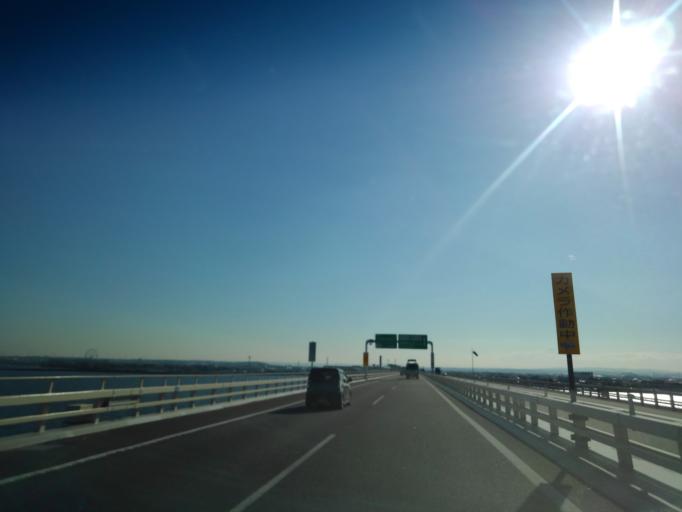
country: JP
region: Chiba
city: Kisarazu
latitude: 35.4412
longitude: 139.9084
